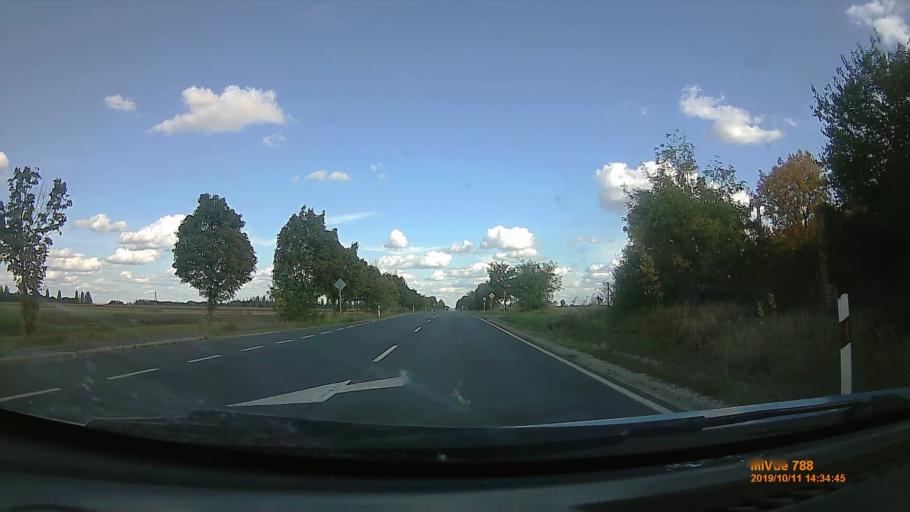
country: HU
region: Hajdu-Bihar
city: Ebes
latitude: 47.5601
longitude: 21.4805
